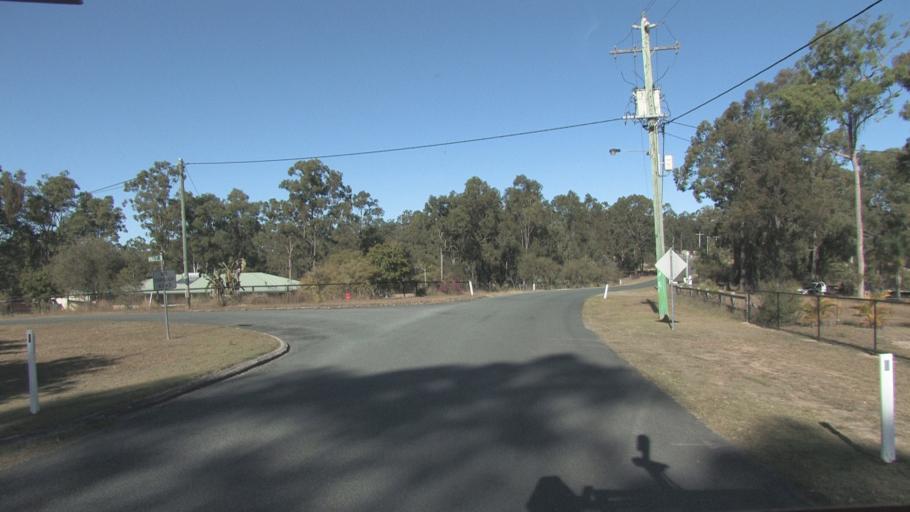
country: AU
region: Queensland
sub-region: Ipswich
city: Springfield Lakes
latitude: -27.6968
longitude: 152.9319
